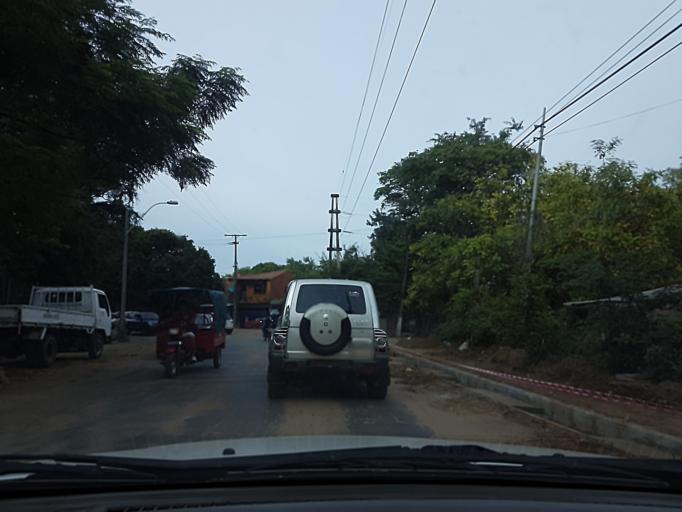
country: PY
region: Asuncion
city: Asuncion
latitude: -25.2505
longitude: -57.5799
